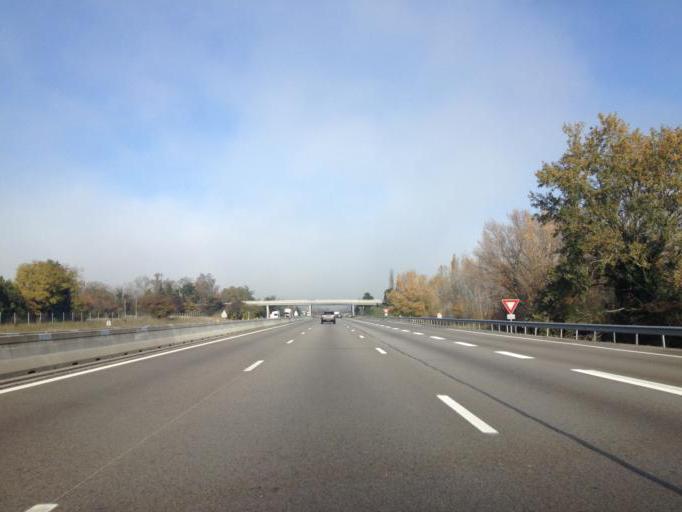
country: FR
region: Rhone-Alpes
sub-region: Departement de la Drome
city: Saint-Marcel-les-Sauzet
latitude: 44.5922
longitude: 4.7997
